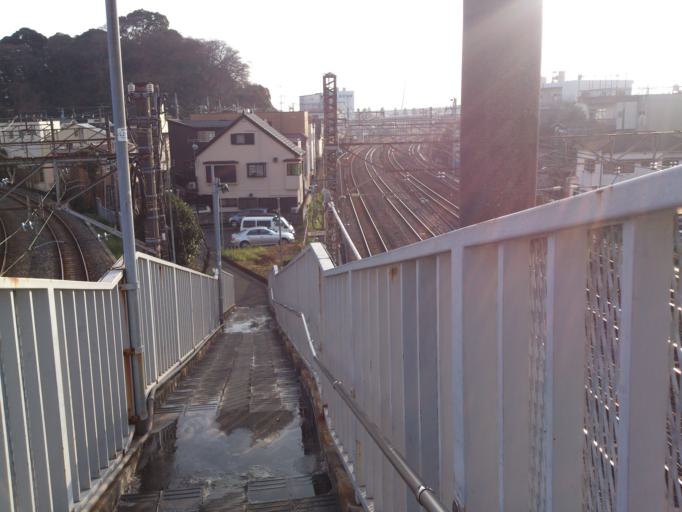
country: JP
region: Chiba
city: Matsudo
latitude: 35.7759
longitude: 139.8977
